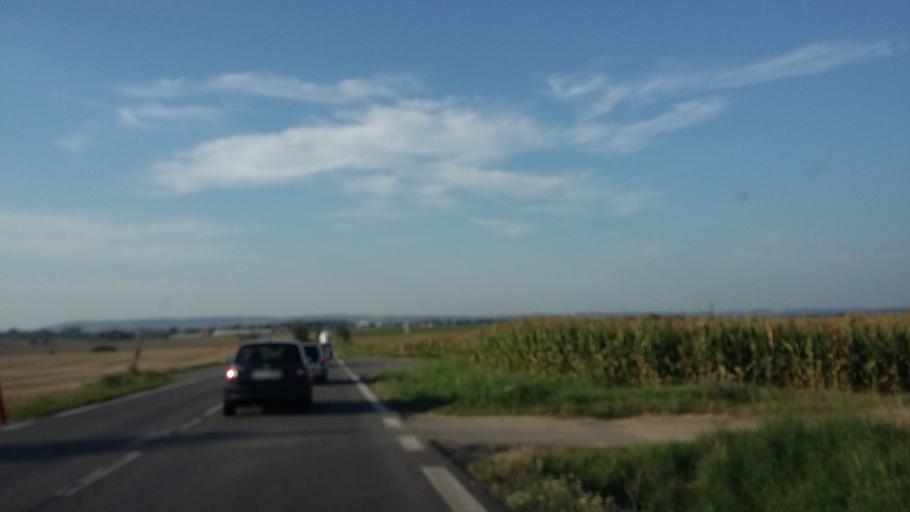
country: CZ
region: Central Bohemia
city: Lustenice
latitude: 50.2848
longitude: 14.9558
